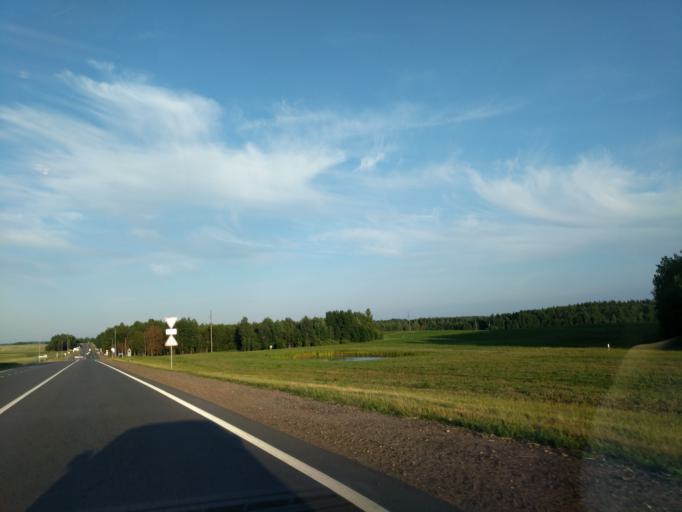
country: BY
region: Minsk
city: Bal'shavik
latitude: 54.0904
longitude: 27.5304
